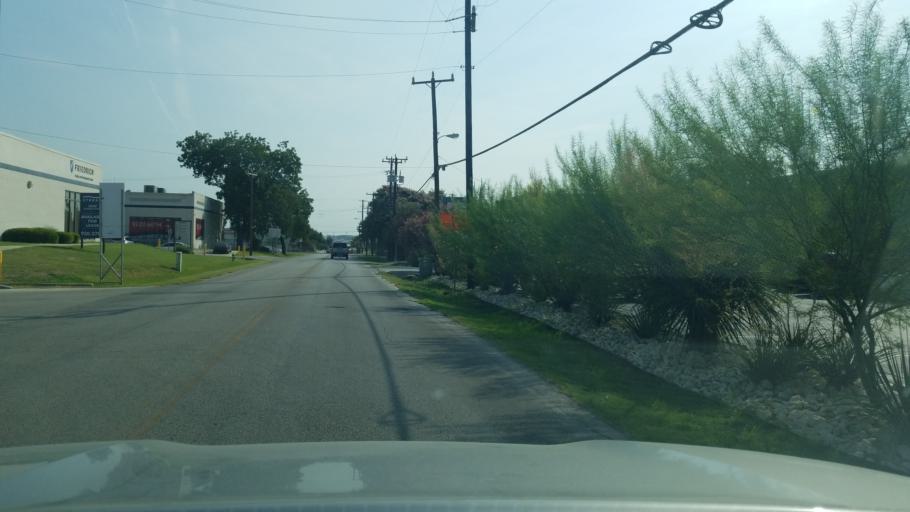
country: US
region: Texas
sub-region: Bexar County
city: Castle Hills
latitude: 29.5353
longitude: -98.4857
